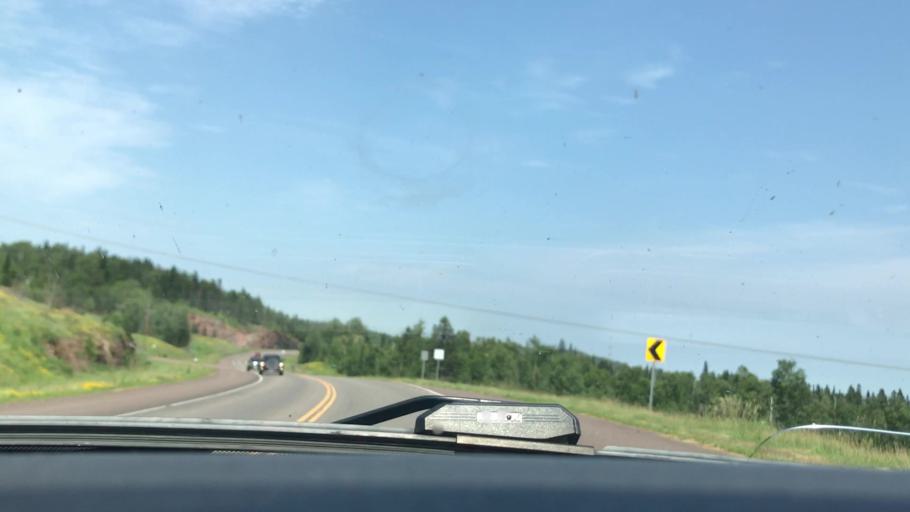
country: US
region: Minnesota
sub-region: Lake County
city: Silver Bay
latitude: 47.3051
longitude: -91.2433
